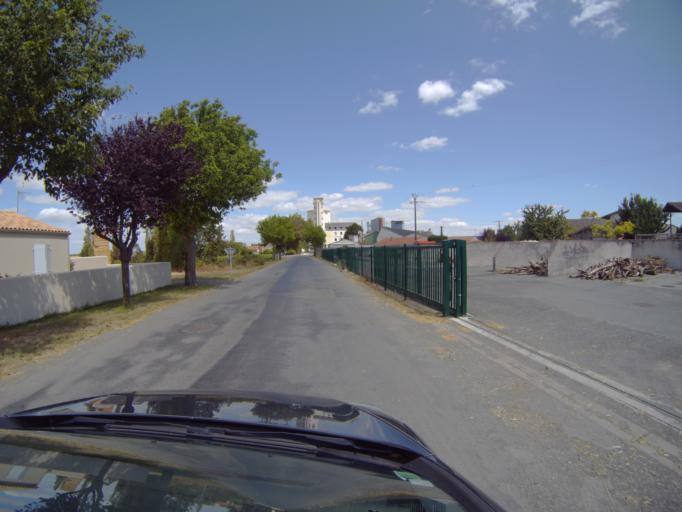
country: FR
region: Poitou-Charentes
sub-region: Departement de la Charente-Maritime
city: Courcon
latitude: 46.2464
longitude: -0.8126
